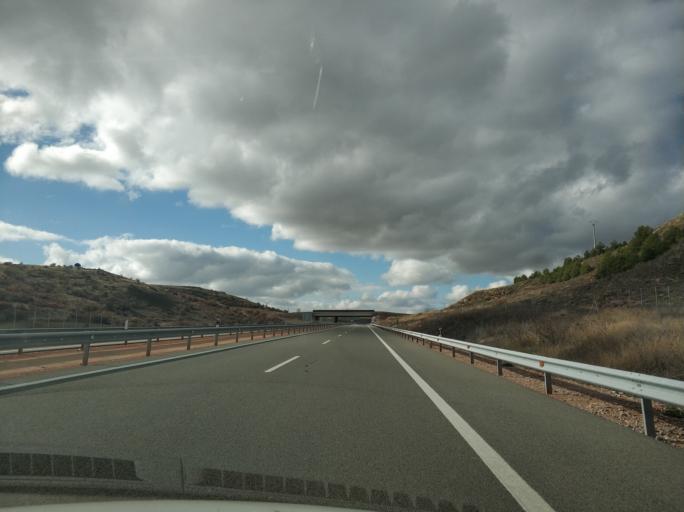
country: ES
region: Castille and Leon
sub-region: Provincia de Soria
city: Medinaceli
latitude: 41.1938
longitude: -2.4416
